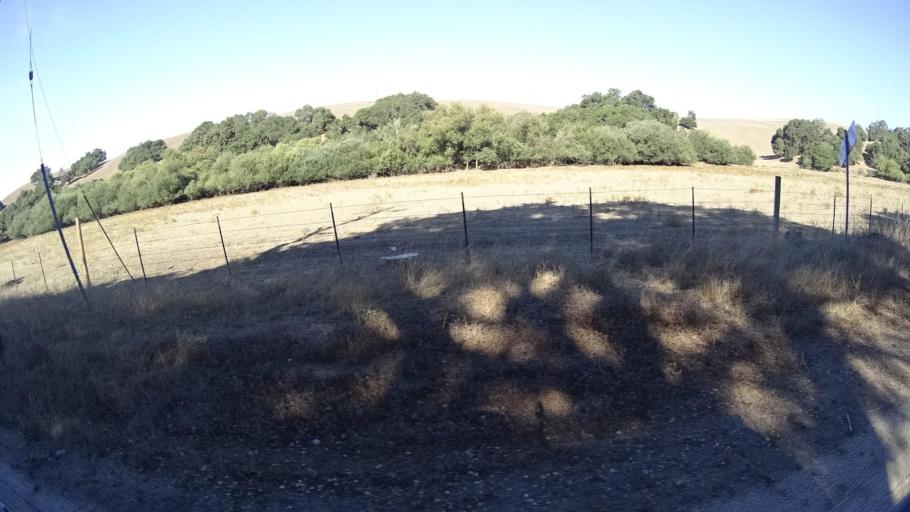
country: US
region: California
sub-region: San Benito County
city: San Juan Bautista
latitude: 36.7916
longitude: -121.5789
